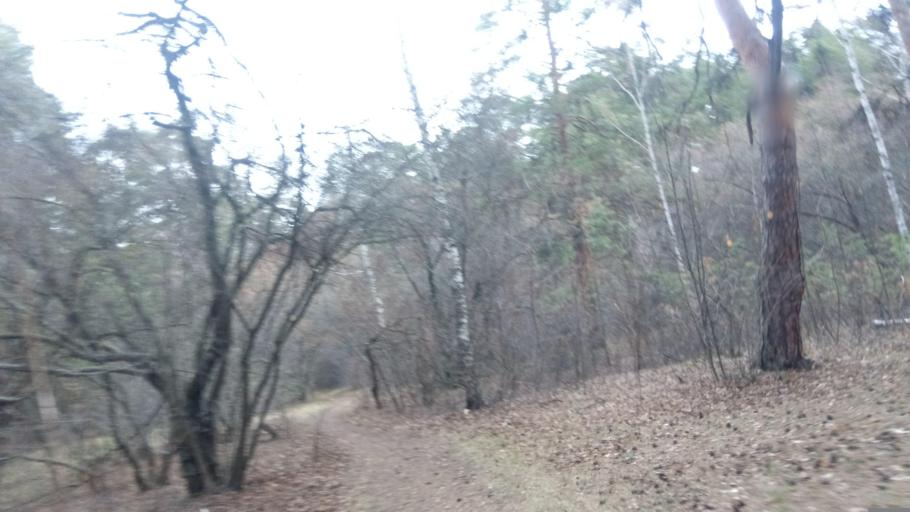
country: RU
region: Chelyabinsk
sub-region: Gorod Chelyabinsk
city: Chelyabinsk
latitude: 55.1502
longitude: 61.3546
